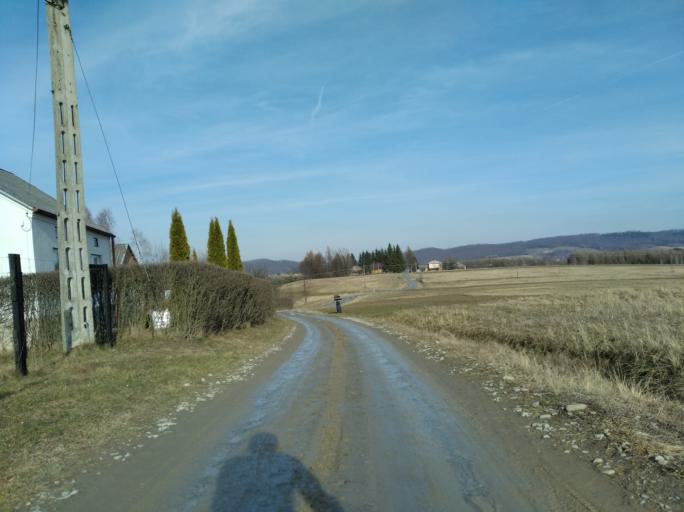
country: PL
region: Subcarpathian Voivodeship
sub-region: Powiat brzozowski
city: Gorki
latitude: 49.6469
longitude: 22.0589
